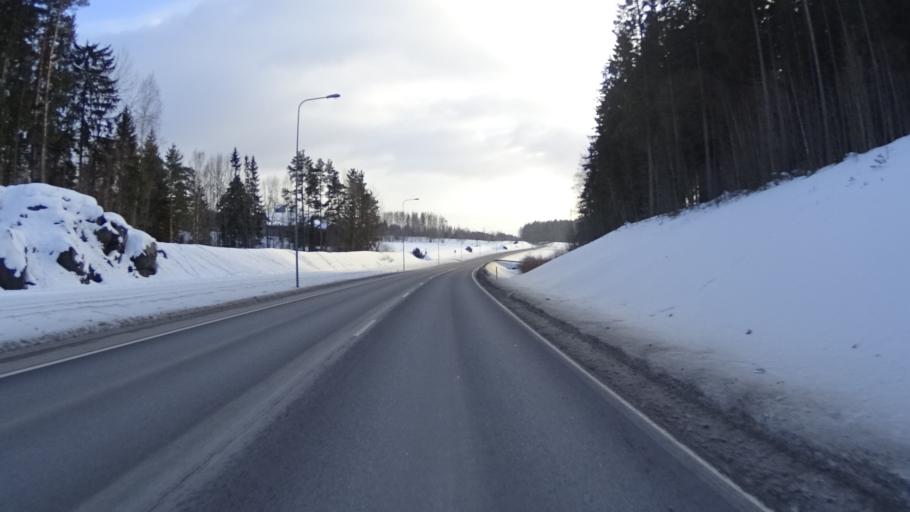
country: FI
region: Uusimaa
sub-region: Helsinki
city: Lohja
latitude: 60.2844
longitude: 24.0597
